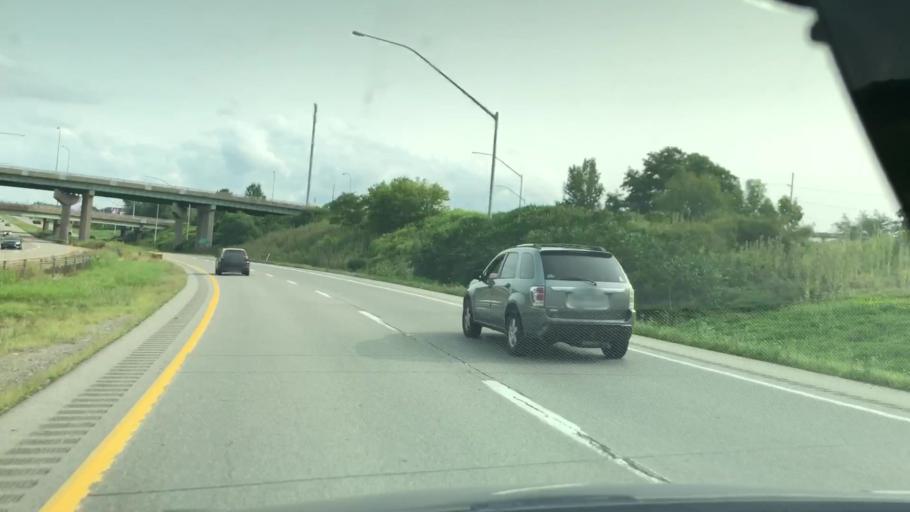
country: US
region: Pennsylvania
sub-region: Erie County
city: Erie
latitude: 42.0956
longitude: -80.1226
